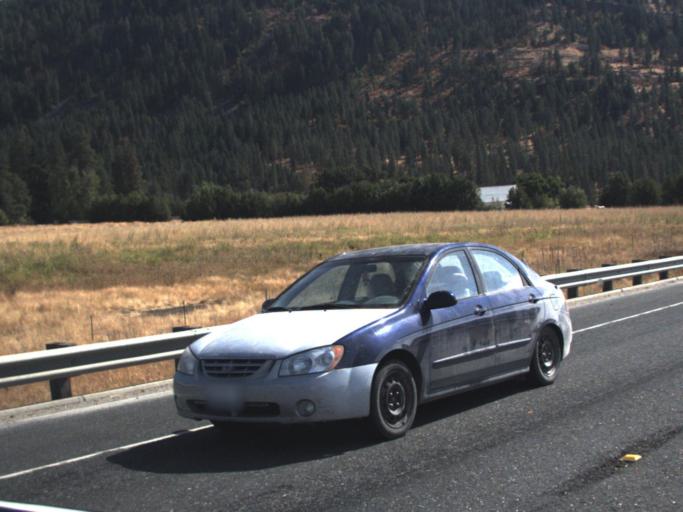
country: US
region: Washington
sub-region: Stevens County
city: Colville
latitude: 48.3922
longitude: -117.8463
